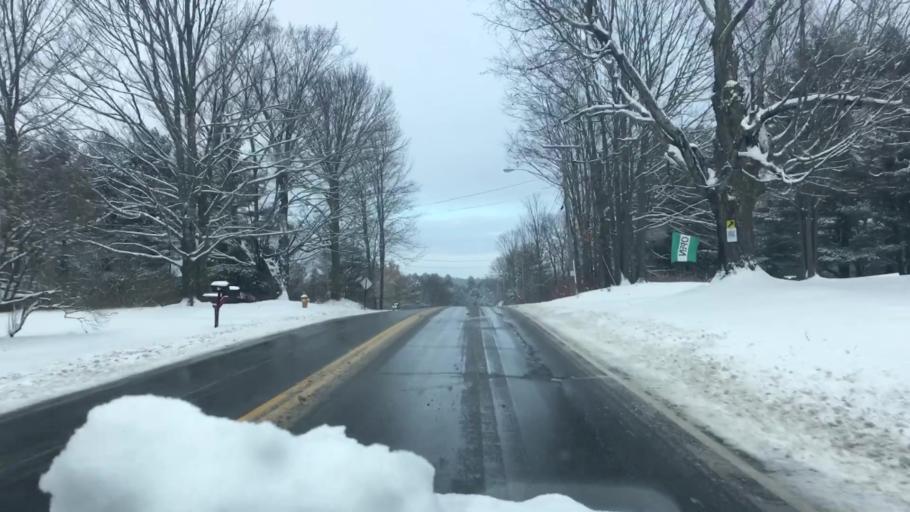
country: US
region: Maine
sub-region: Cumberland County
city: Westbrook
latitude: 43.6997
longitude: -70.3743
